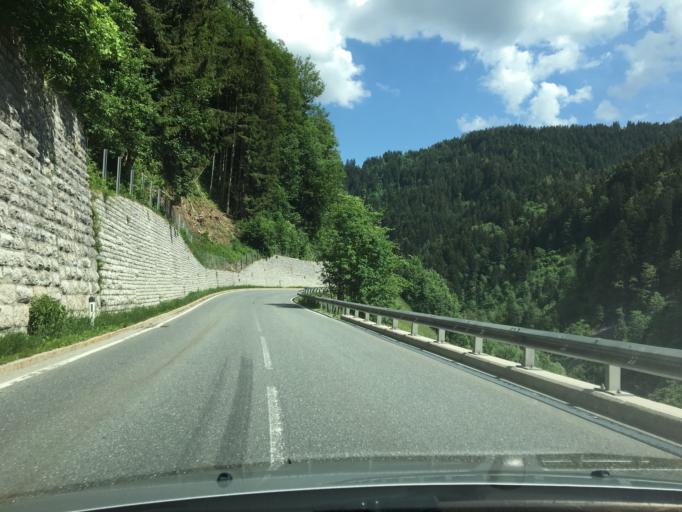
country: AT
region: Salzburg
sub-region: Politischer Bezirk Sankt Johann im Pongau
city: Sankt Johann im Pongau
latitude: 47.3325
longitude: 13.2255
